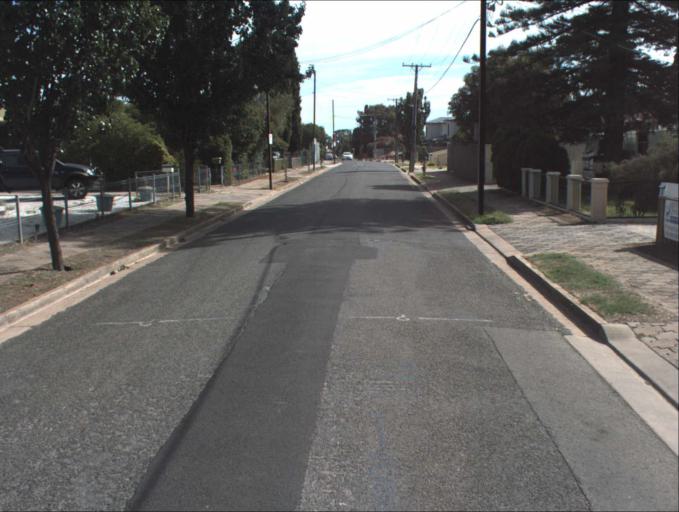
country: AU
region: South Australia
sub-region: Port Adelaide Enfield
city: Klemzig
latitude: -34.8671
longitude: 138.6441
